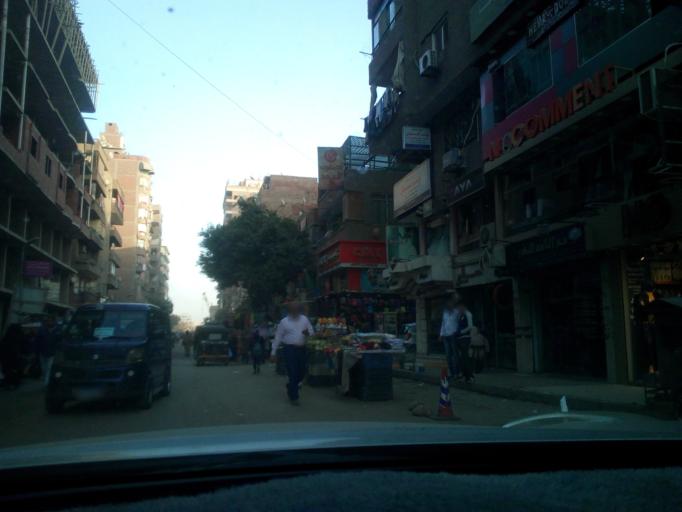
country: EG
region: Muhafazat al Qalyubiyah
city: Al Khankah
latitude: 30.1280
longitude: 31.3489
